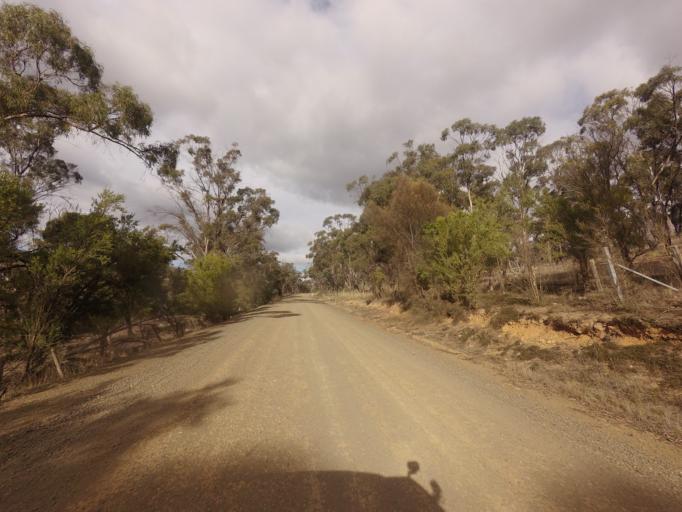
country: AU
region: Tasmania
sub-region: Brighton
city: Bridgewater
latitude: -42.4544
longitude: 147.2464
